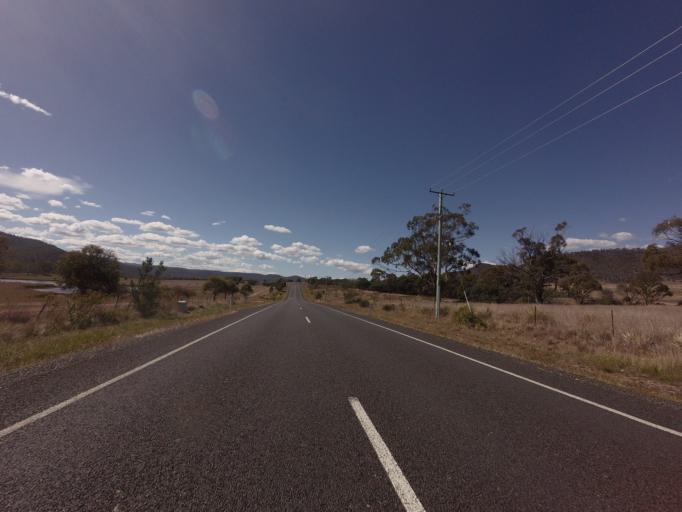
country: AU
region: Tasmania
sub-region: Break O'Day
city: St Helens
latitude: -41.7159
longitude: 147.8356
